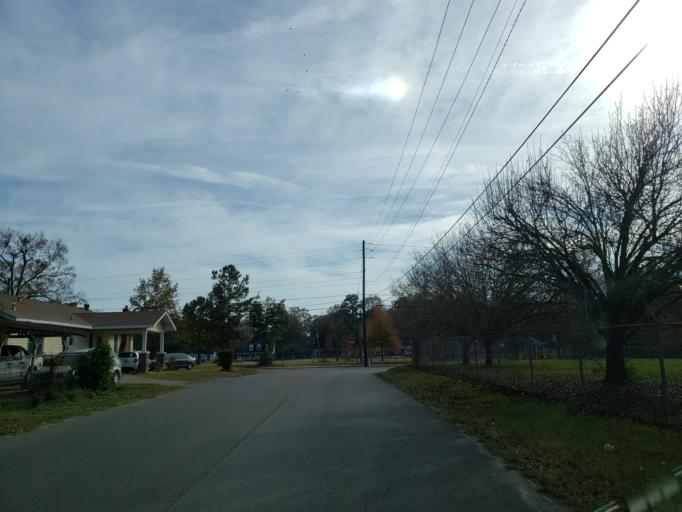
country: US
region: Mississippi
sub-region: Forrest County
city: Hattiesburg
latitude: 31.3362
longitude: -89.3043
